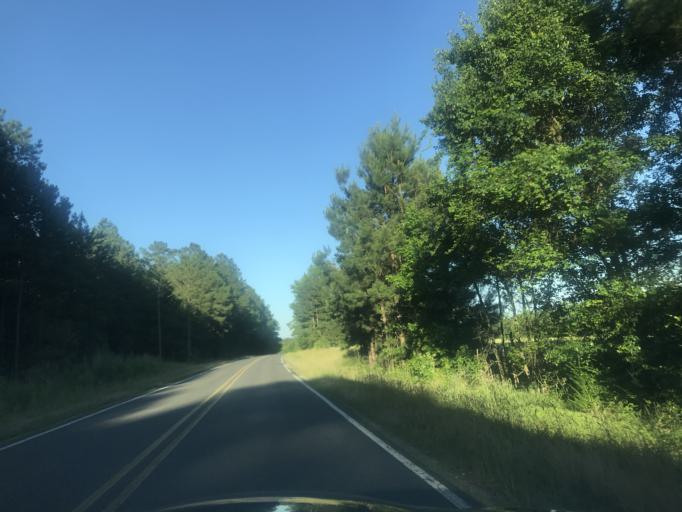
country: US
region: North Carolina
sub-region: Johnston County
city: Archer Lodge
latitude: 35.7291
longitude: -78.4336
